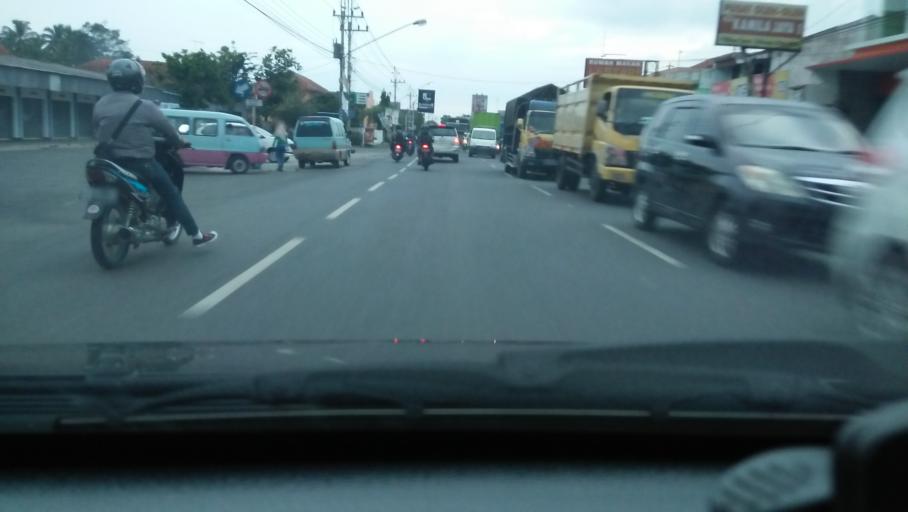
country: ID
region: Central Java
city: Magelang
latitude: -7.3932
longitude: 110.2467
